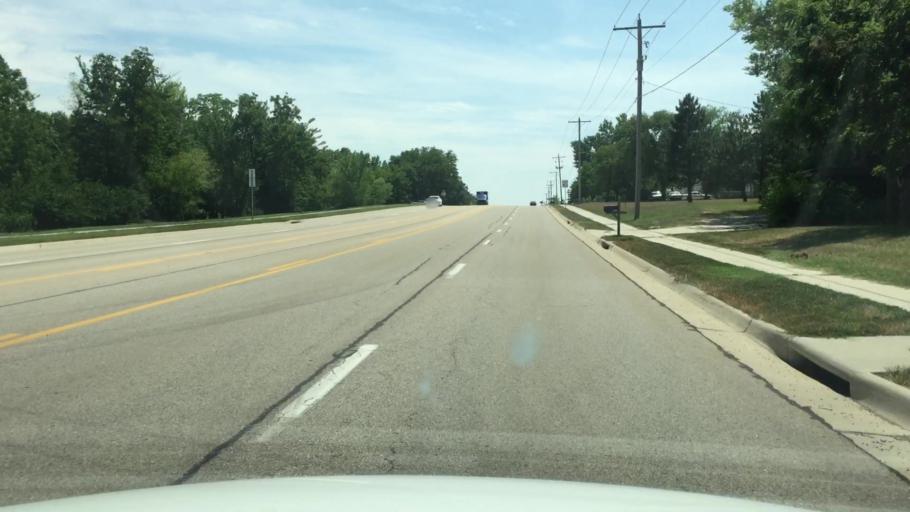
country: US
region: Kansas
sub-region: Shawnee County
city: Topeka
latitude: 39.0005
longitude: -95.6145
